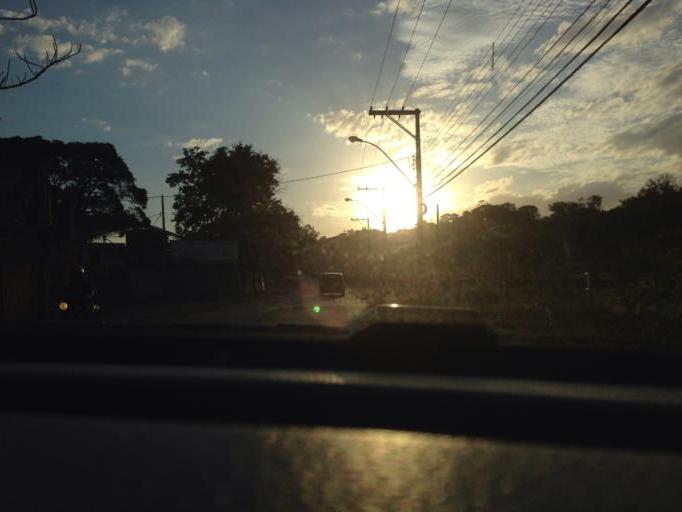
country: BR
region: Espirito Santo
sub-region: Guarapari
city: Guarapari
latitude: -20.6270
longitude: -40.4740
